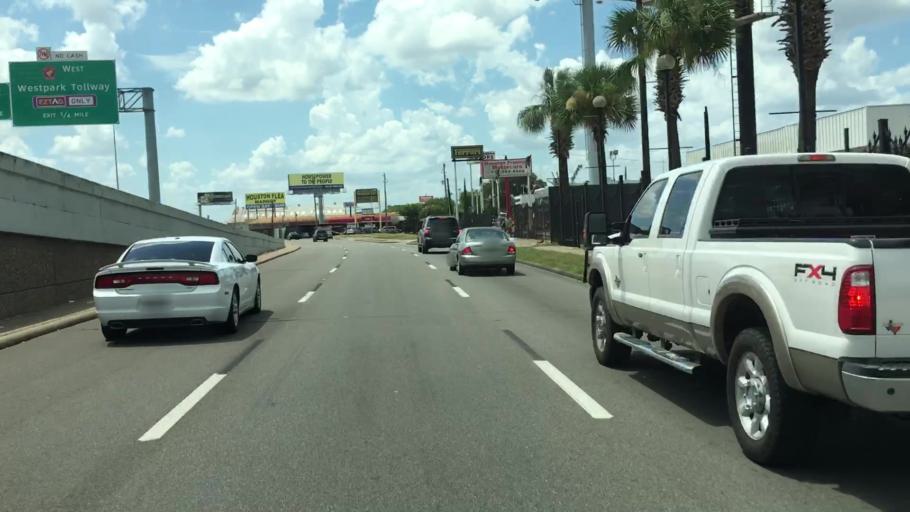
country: US
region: Texas
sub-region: Harris County
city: Bellaire
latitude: 29.7262
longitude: -95.4862
